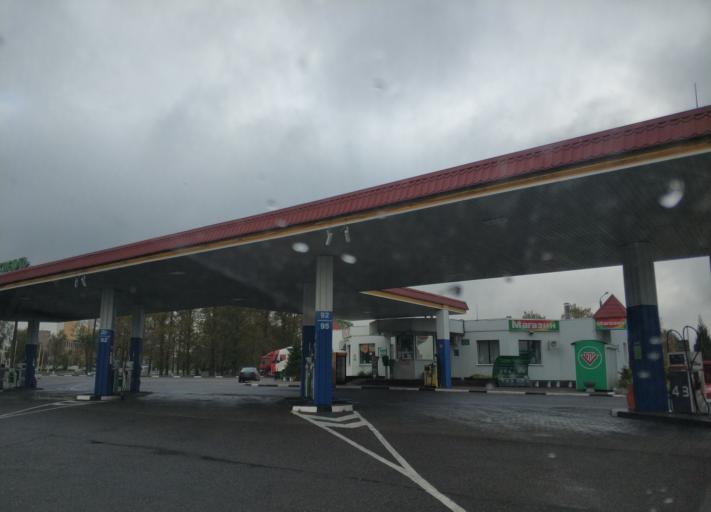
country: BY
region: Vitebsk
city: Vitebsk
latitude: 55.1930
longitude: 30.1405
